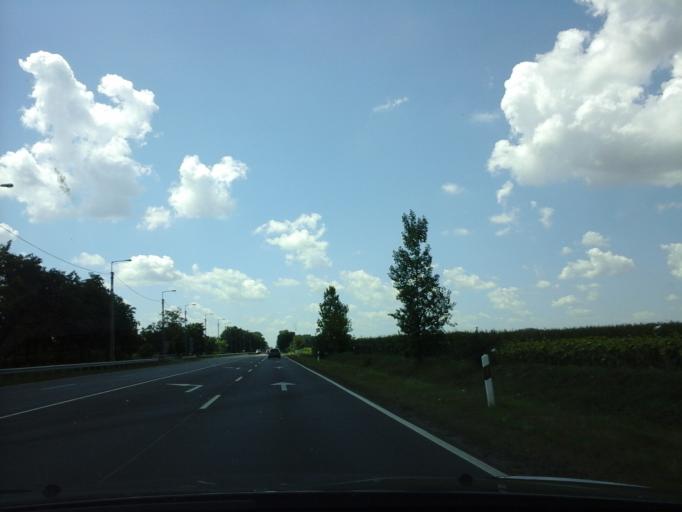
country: HU
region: Hajdu-Bihar
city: Ebes
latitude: 47.4824
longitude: 21.5026
